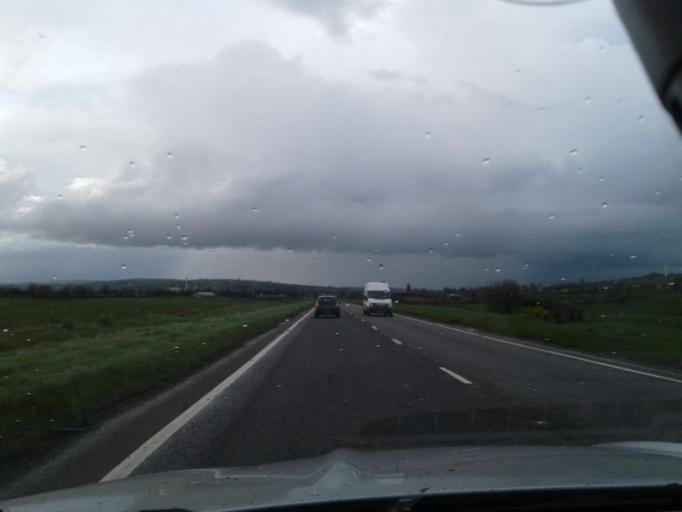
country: GB
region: Northern Ireland
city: Newtownstewart
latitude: 54.7263
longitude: -7.4054
